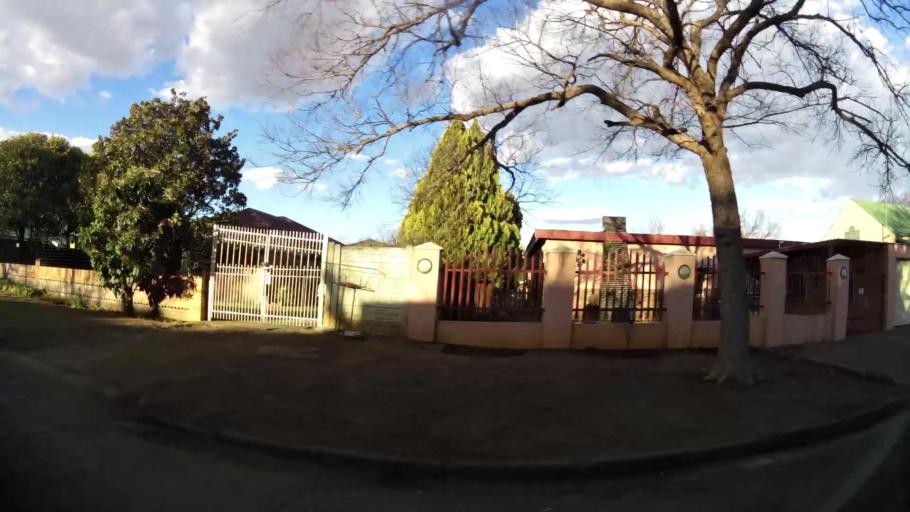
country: ZA
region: North-West
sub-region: Dr Kenneth Kaunda District Municipality
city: Potchefstroom
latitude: -26.7257
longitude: 27.1002
